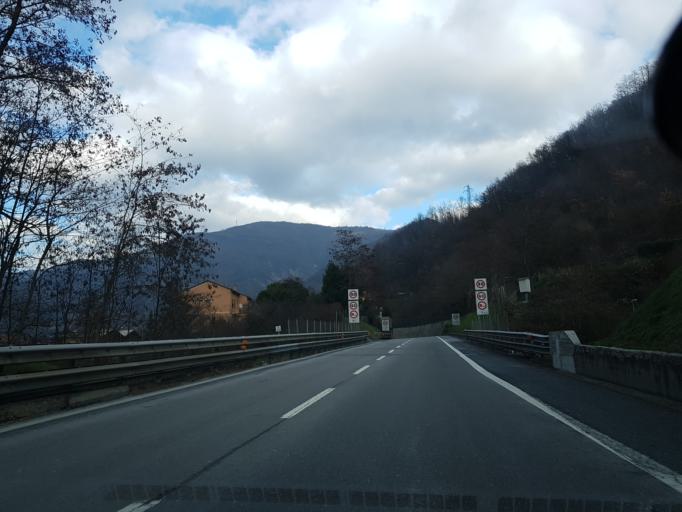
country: IT
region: Liguria
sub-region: Provincia di Genova
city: Isola del Cantone
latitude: 44.6405
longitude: 8.9558
